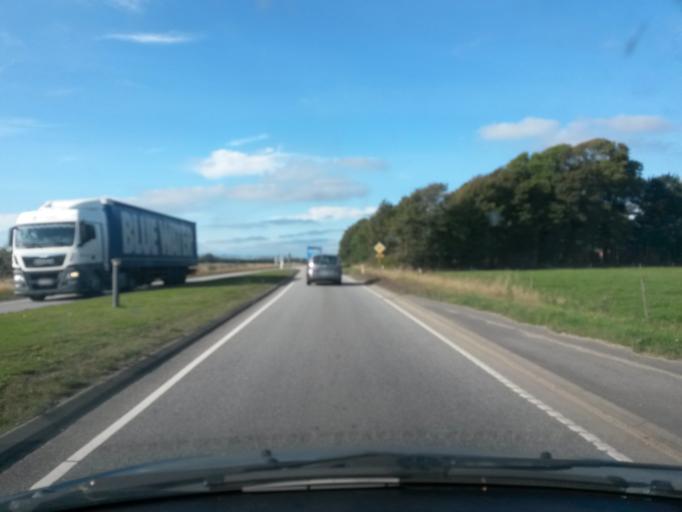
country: DK
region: Central Jutland
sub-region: Herning Kommune
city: Avlum
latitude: 56.2656
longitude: 8.7734
